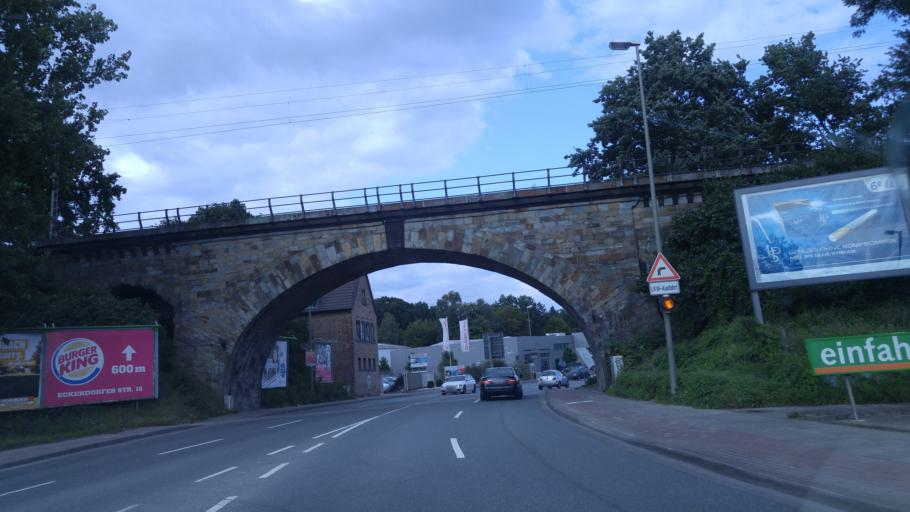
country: DE
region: North Rhine-Westphalia
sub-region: Regierungsbezirk Detmold
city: Bielefeld
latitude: 52.0318
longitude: 8.5458
